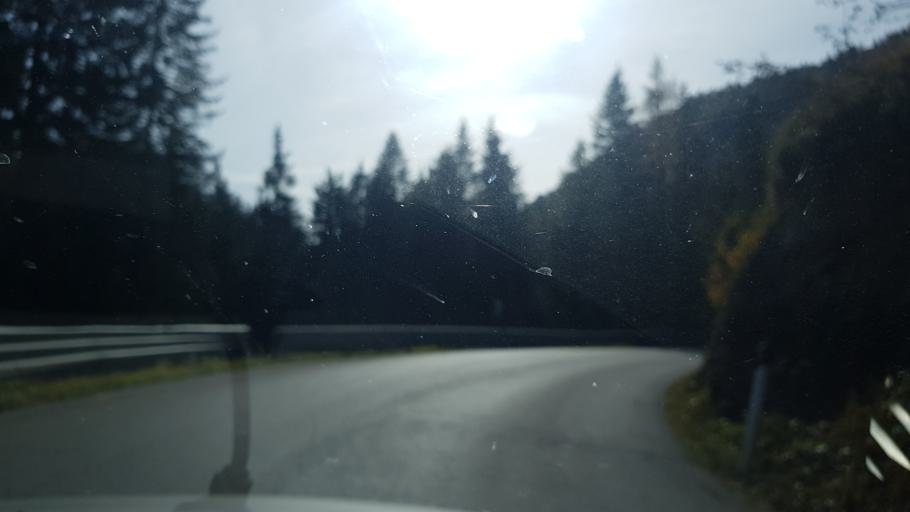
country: IT
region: Veneto
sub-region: Provincia di Belluno
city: Auronzo
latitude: 46.6505
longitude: 12.4300
